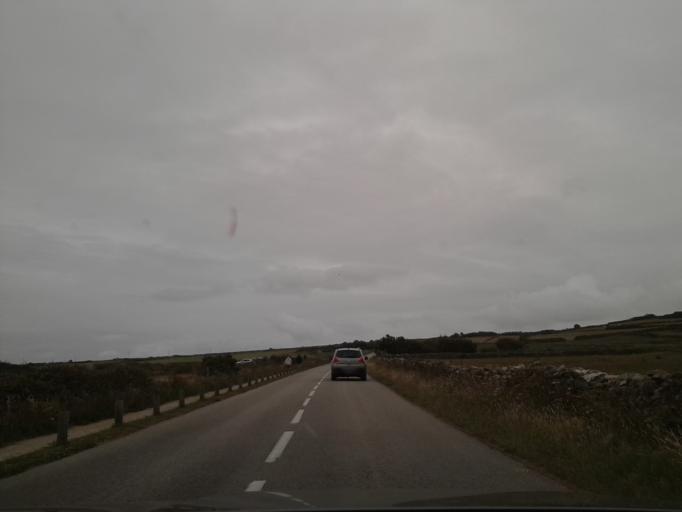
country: FR
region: Lower Normandy
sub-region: Departement de la Manche
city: Beaumont-Hague
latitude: 49.7159
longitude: -1.9432
